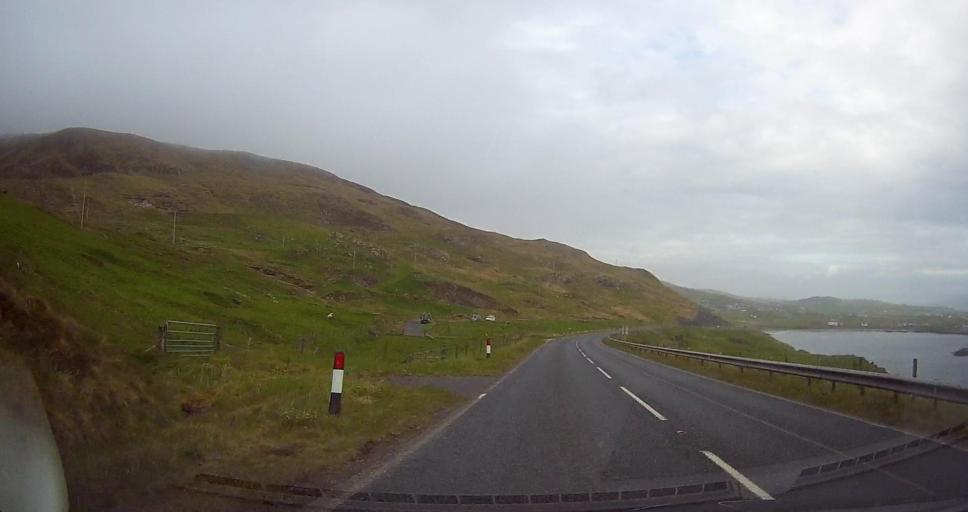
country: GB
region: Scotland
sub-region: Shetland Islands
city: Sandwick
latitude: 60.0247
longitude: -1.2366
